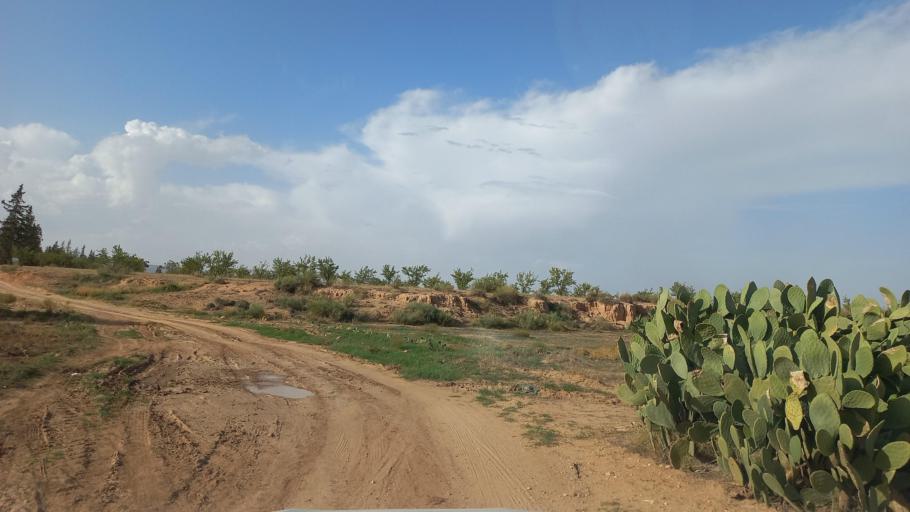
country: TN
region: Al Qasrayn
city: Kasserine
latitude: 35.2284
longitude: 8.9679
